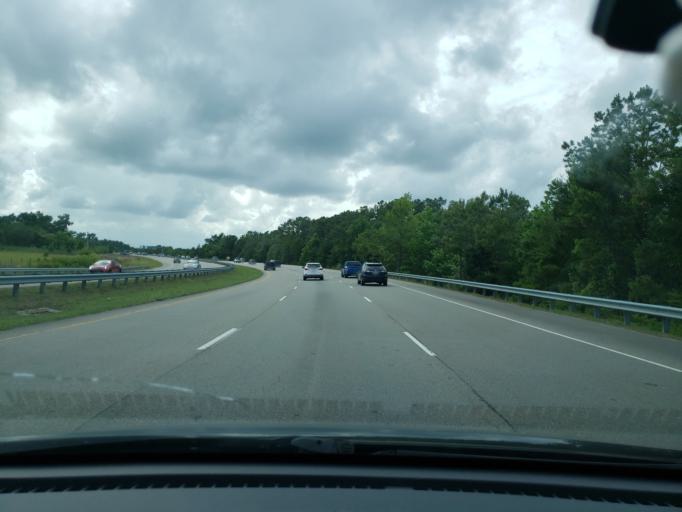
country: US
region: North Carolina
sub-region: New Hanover County
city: Wrightsboro
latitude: 34.2568
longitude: -77.9063
